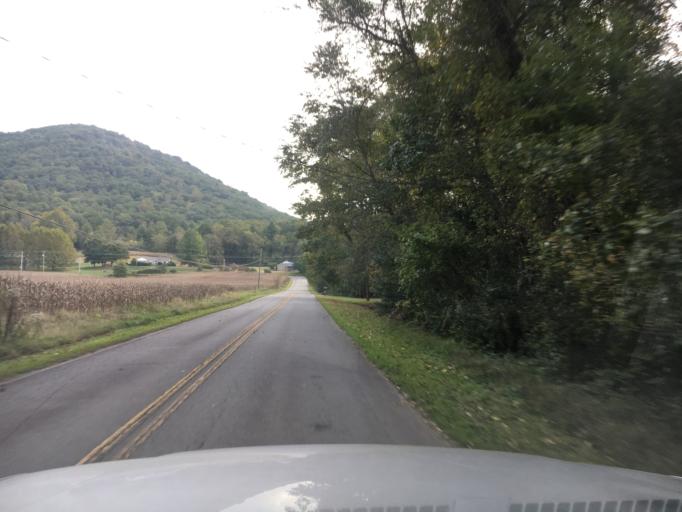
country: US
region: North Carolina
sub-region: Buncombe County
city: Swannanoa
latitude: 35.6087
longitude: -82.4179
